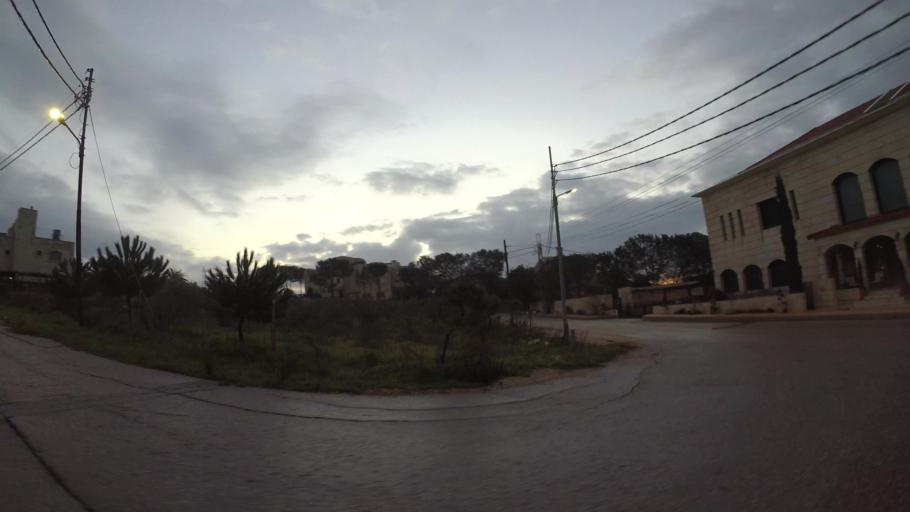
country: JO
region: Amman
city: Al Jubayhah
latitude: 32.0311
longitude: 35.8108
